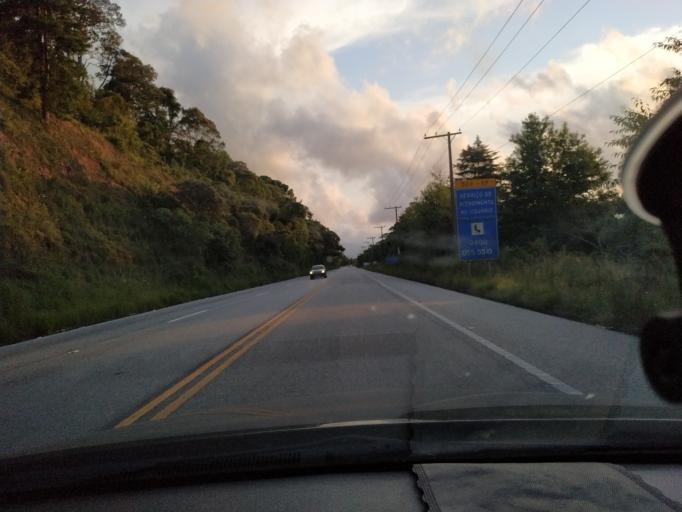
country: BR
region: Sao Paulo
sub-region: Campos Do Jordao
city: Campos do Jordao
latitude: -22.7700
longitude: -45.6148
